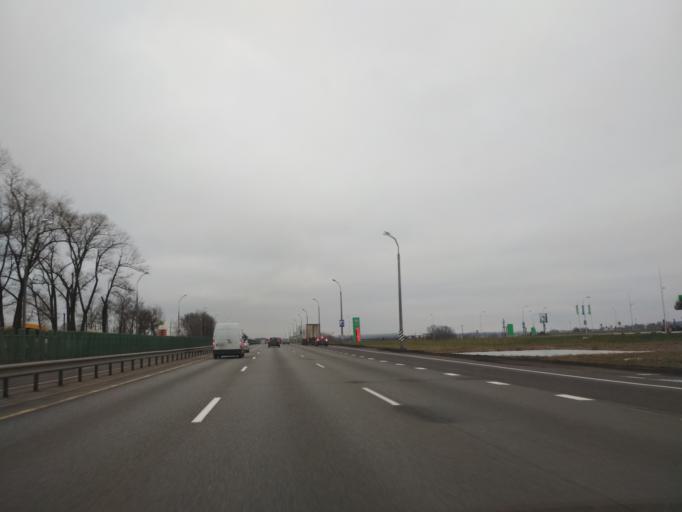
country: BY
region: Minsk
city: Yubilyeyny
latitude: 53.8378
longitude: 27.5117
